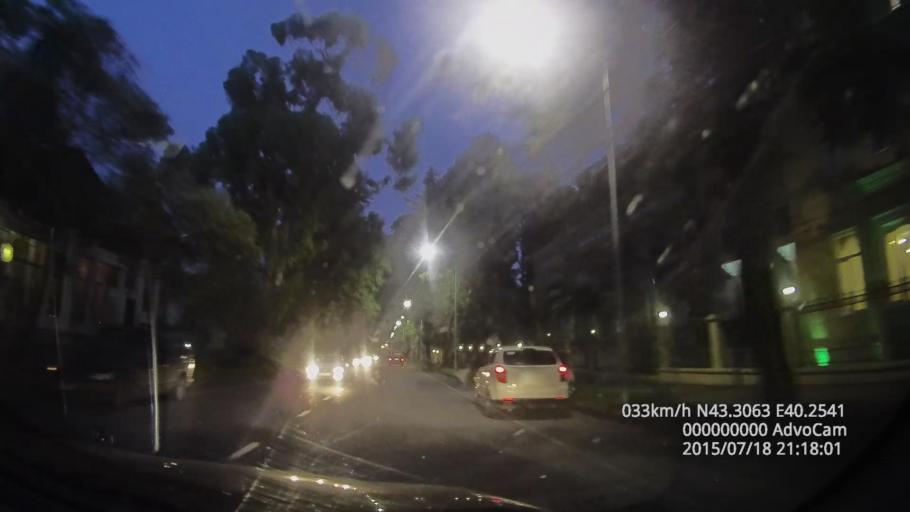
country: GE
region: Abkhazia
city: Gagra
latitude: 43.3061
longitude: 40.2542
